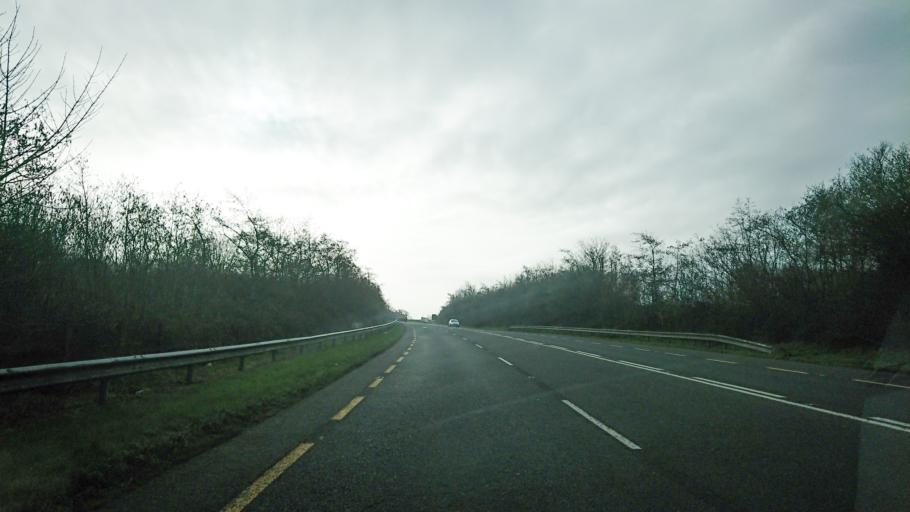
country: IE
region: Munster
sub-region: County Cork
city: Youghal
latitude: 51.9591
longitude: -7.8811
